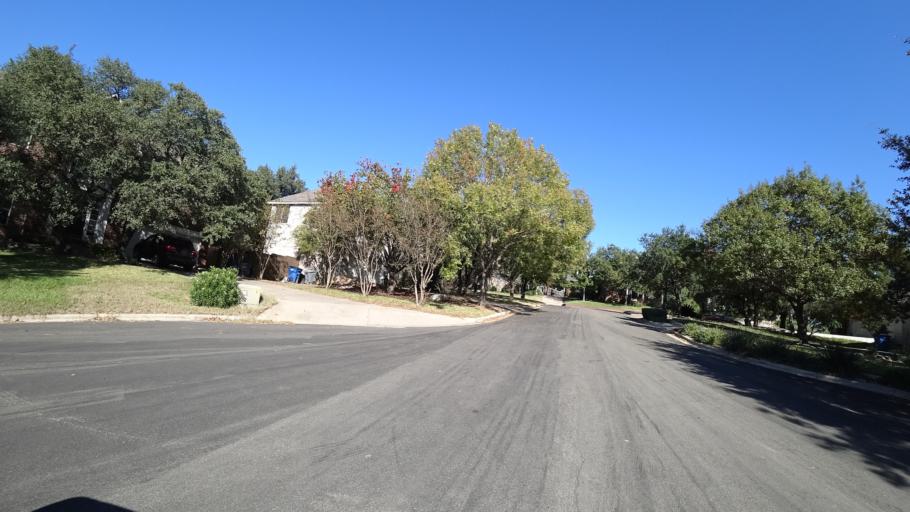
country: US
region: Texas
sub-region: Williamson County
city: Jollyville
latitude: 30.4127
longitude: -97.7719
